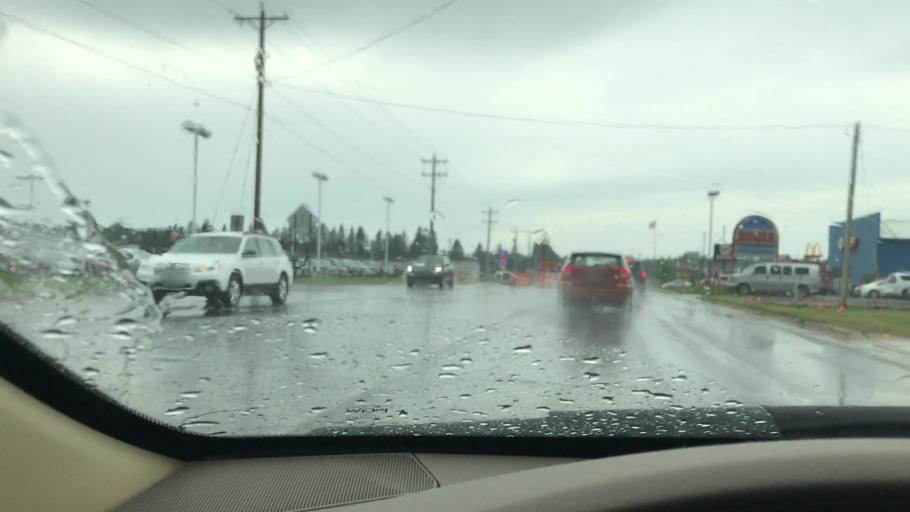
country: US
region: Minnesota
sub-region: Saint Louis County
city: Hermantown
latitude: 46.8223
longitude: -92.1824
